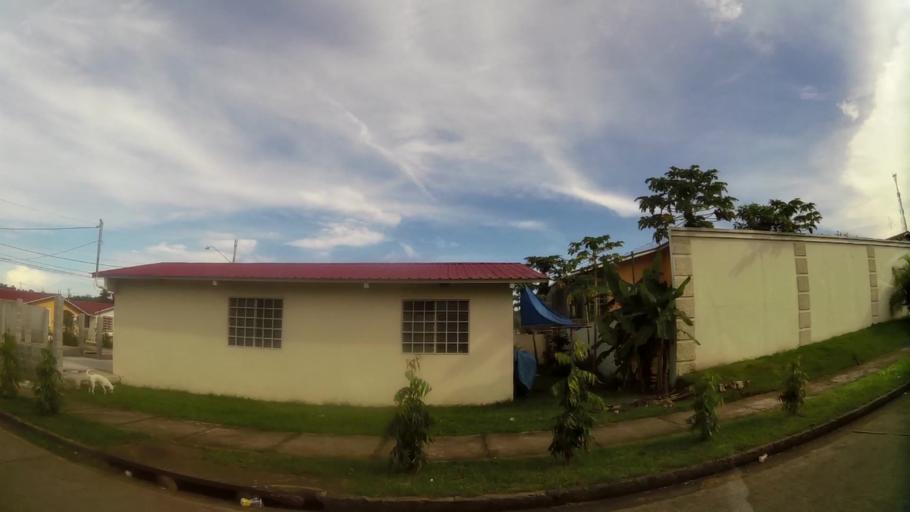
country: PA
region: Panama
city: La Chorrera
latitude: 8.8805
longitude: -79.7630
